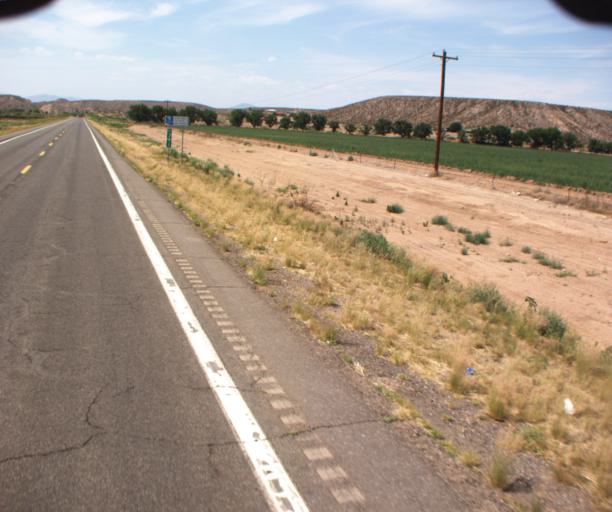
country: US
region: Arizona
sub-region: Greenlee County
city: Clifton
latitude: 32.8584
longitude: -109.1837
